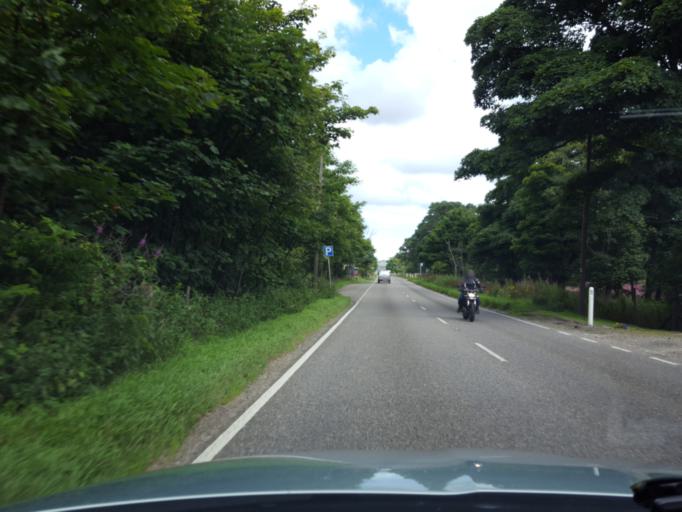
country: GB
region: Scotland
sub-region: Moray
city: Elgin
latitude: 57.6056
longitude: -3.2899
